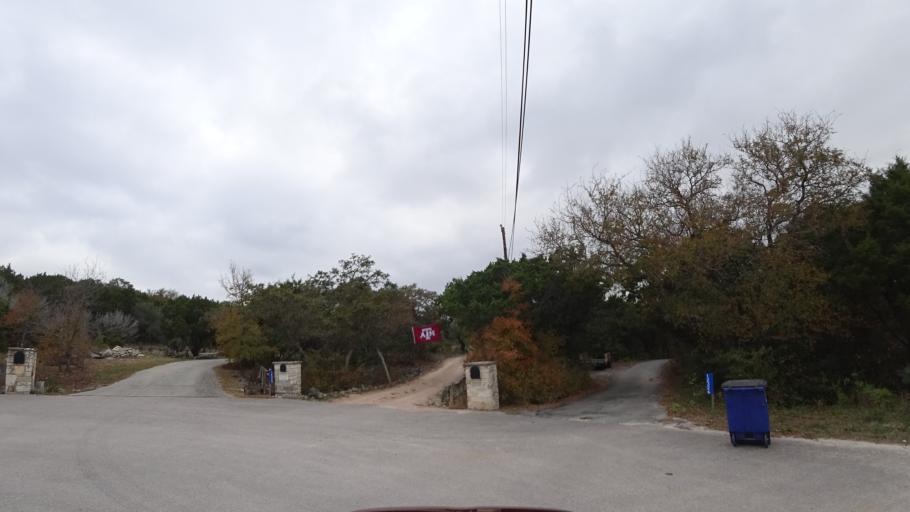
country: US
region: Texas
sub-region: Williamson County
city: Anderson Mill
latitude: 30.4486
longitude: -97.8408
